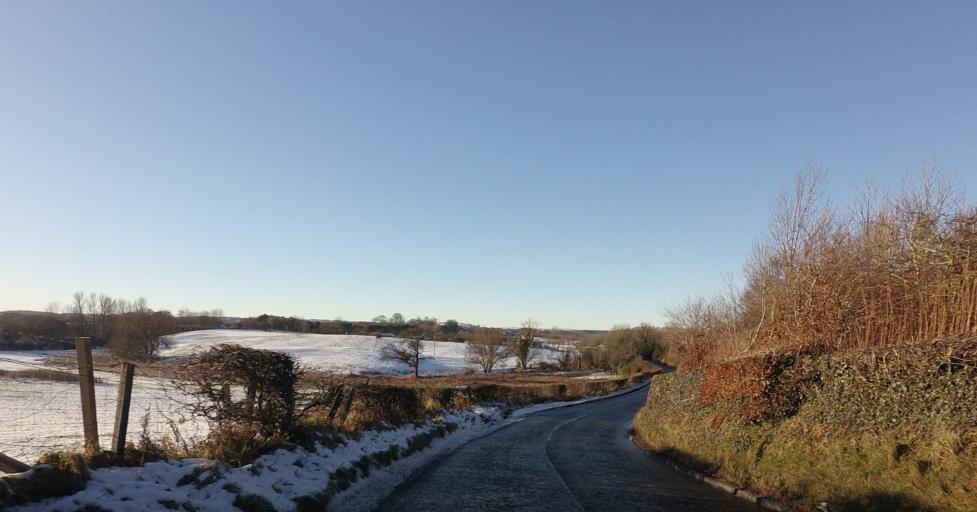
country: GB
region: Scotland
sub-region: West Lothian
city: Linlithgow
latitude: 55.9836
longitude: -3.6186
